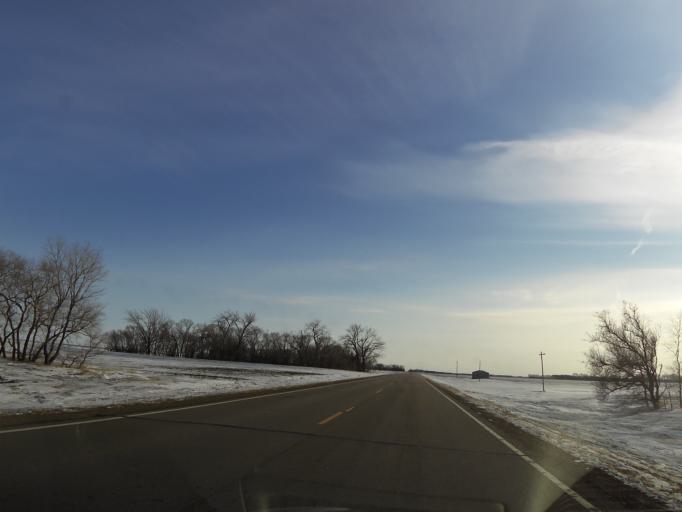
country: US
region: Minnesota
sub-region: Kittson County
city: Hallock
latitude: 48.5518
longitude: -97.1069
